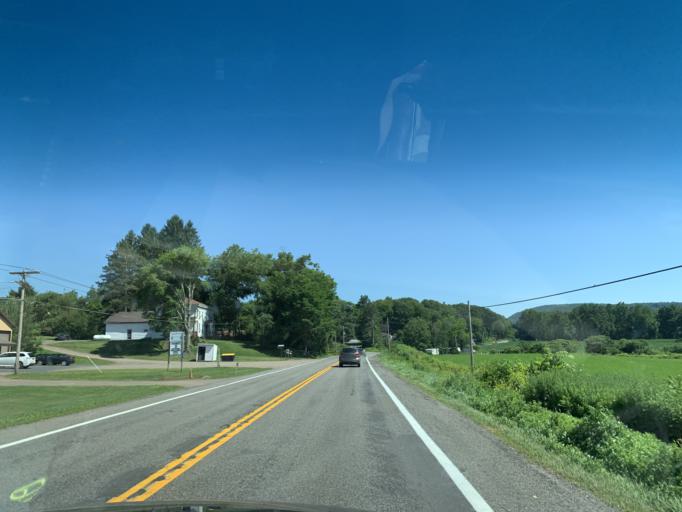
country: US
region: New York
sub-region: Delaware County
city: Sidney
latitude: 42.3340
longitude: -75.4084
